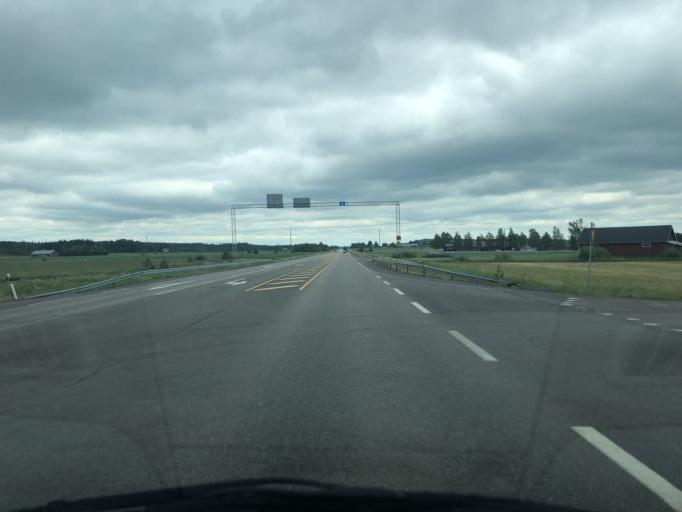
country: FI
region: Kymenlaakso
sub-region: Kouvola
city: Elimaeki
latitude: 60.7428
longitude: 26.4483
